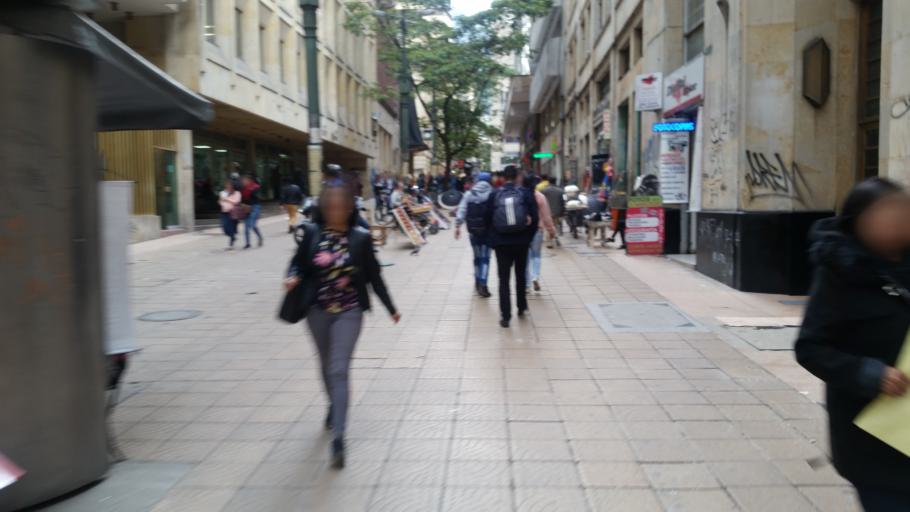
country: CO
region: Bogota D.C.
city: Bogota
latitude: 4.6019
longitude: -74.0754
